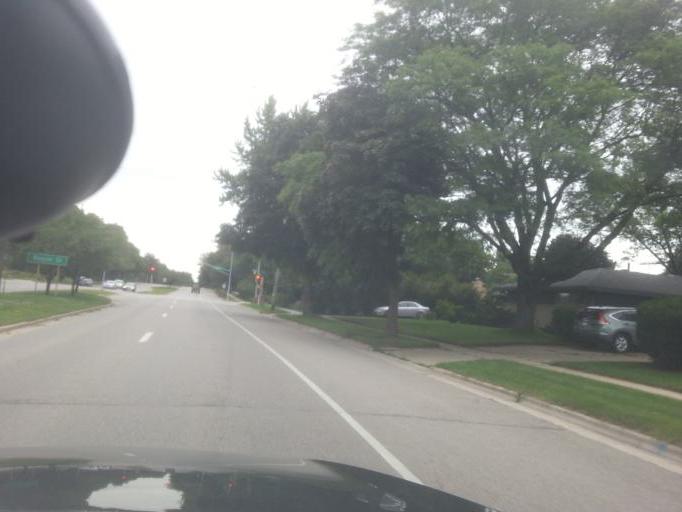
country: US
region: Wisconsin
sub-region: Dane County
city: Shorewood Hills
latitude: 43.0673
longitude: -89.4683
